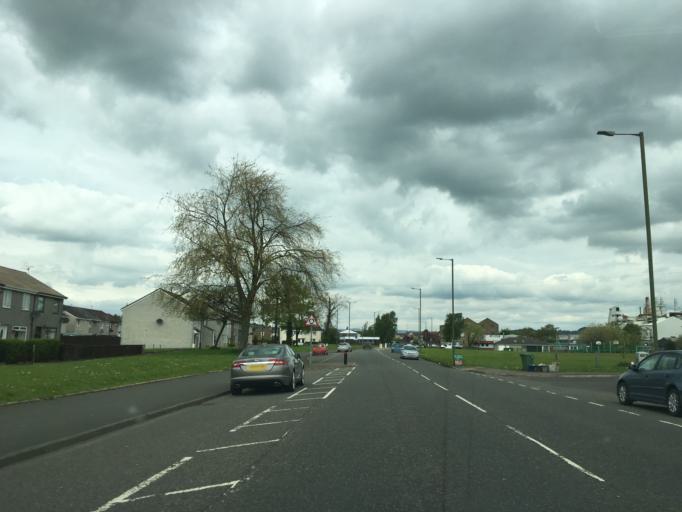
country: GB
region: Scotland
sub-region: Stirling
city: Stirling
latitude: 56.1073
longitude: -3.9257
